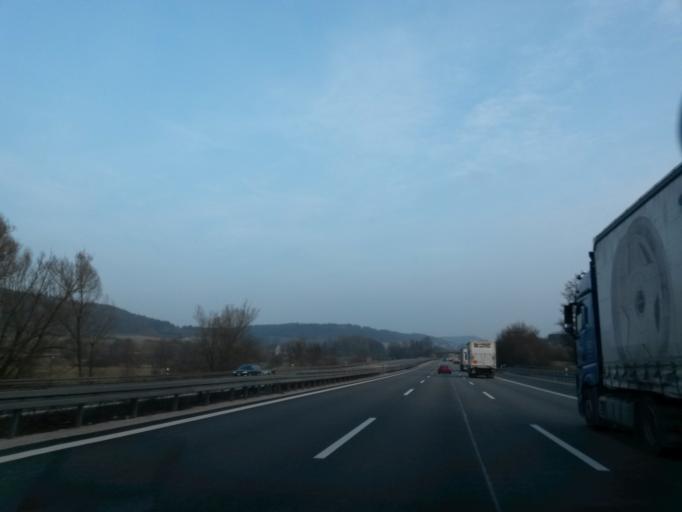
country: DE
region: Bavaria
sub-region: Regierungsbezirk Mittelfranken
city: Greding
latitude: 49.0650
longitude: 11.3158
